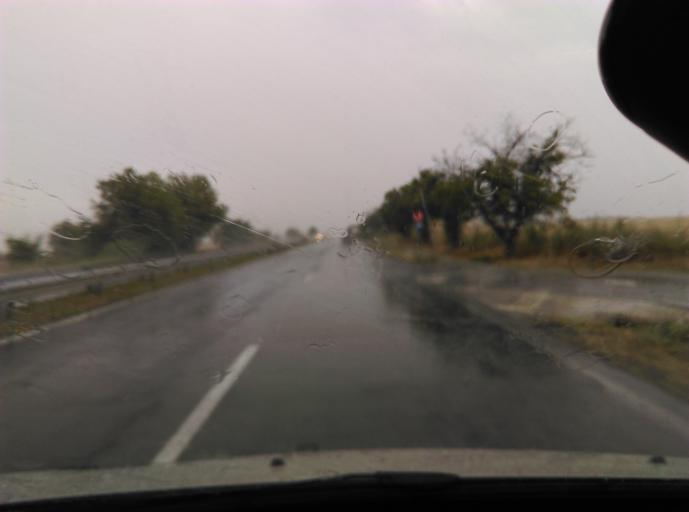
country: BG
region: Burgas
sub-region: Obshtina Burgas
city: Burgas
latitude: 42.5727
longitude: 27.4125
